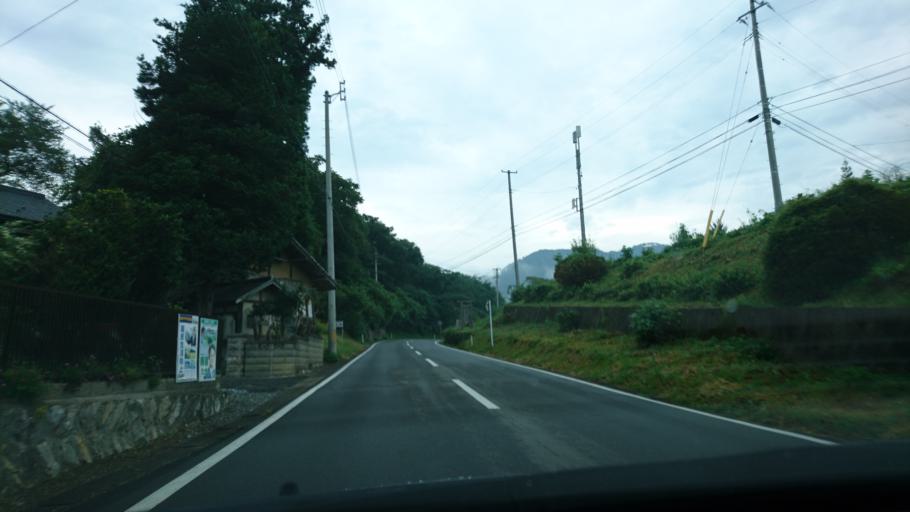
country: JP
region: Iwate
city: Ichinoseki
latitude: 38.9512
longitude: 141.2522
